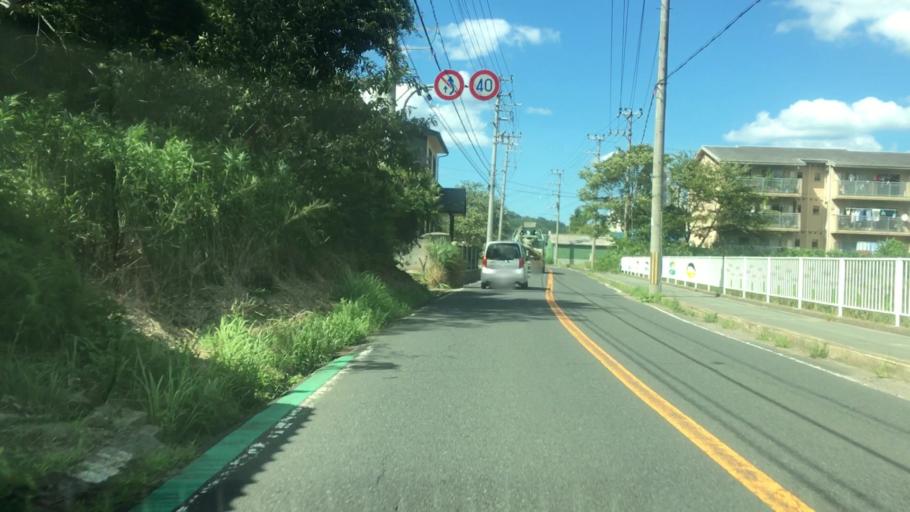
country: JP
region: Kyoto
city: Miyazu
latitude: 35.6147
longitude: 135.0538
